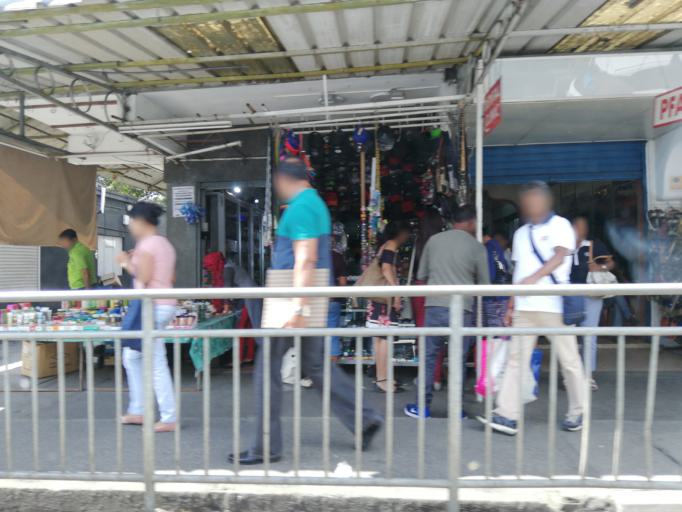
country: MU
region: Flacq
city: Centre de Flacq
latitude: -20.1924
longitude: 57.7235
